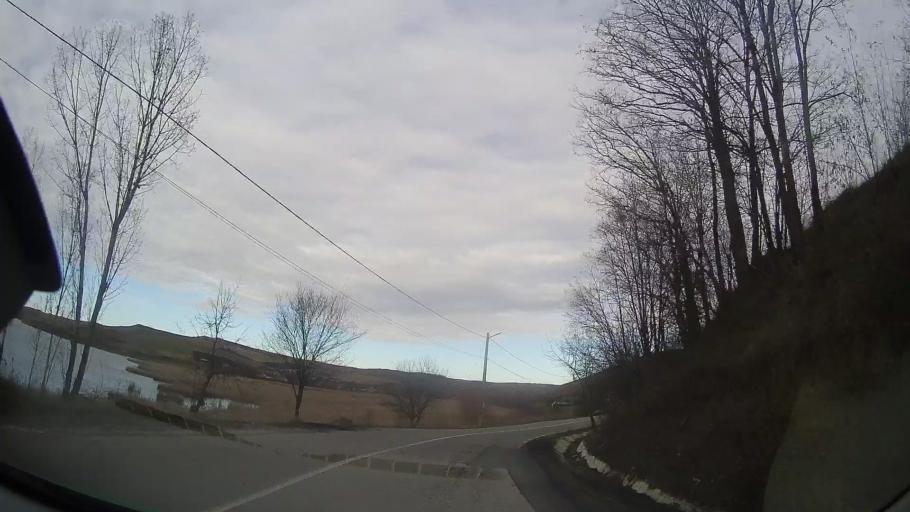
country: RO
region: Cluj
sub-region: Comuna Geaca
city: Geaca
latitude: 46.8387
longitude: 24.1344
